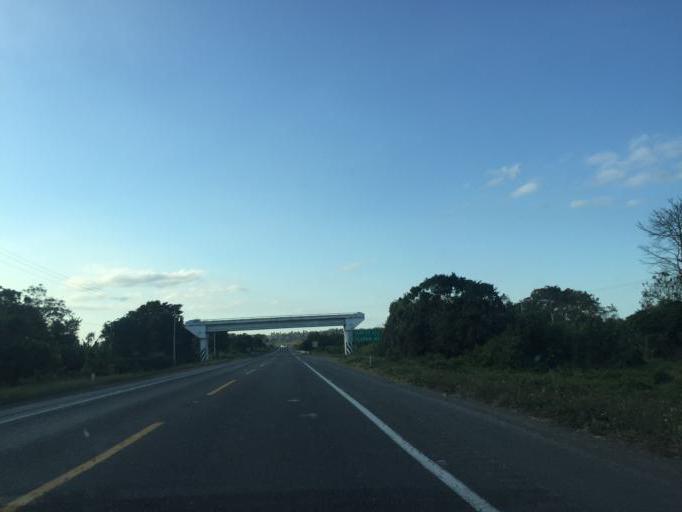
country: MX
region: Veracruz
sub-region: Papantla
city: Residencial Tajin
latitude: 20.6298
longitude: -97.3945
